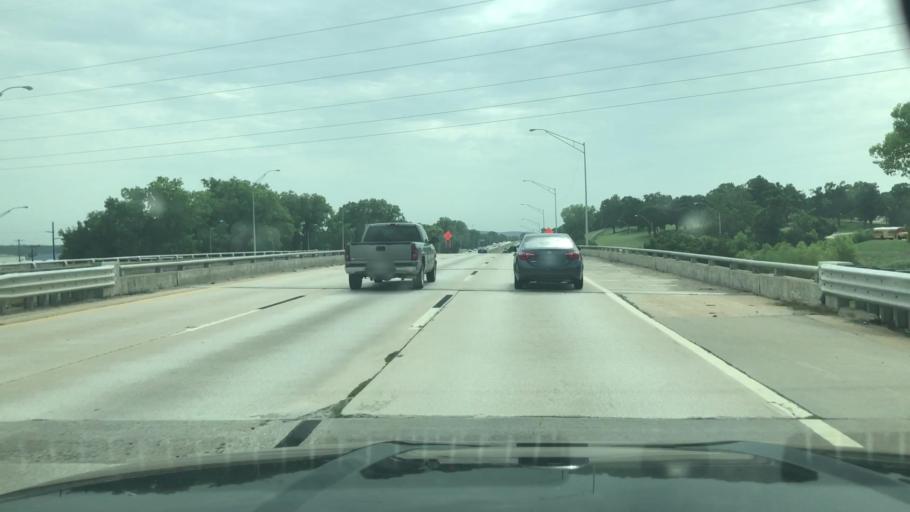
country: US
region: Oklahoma
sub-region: Tulsa County
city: Sand Springs
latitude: 36.1433
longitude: -96.0829
